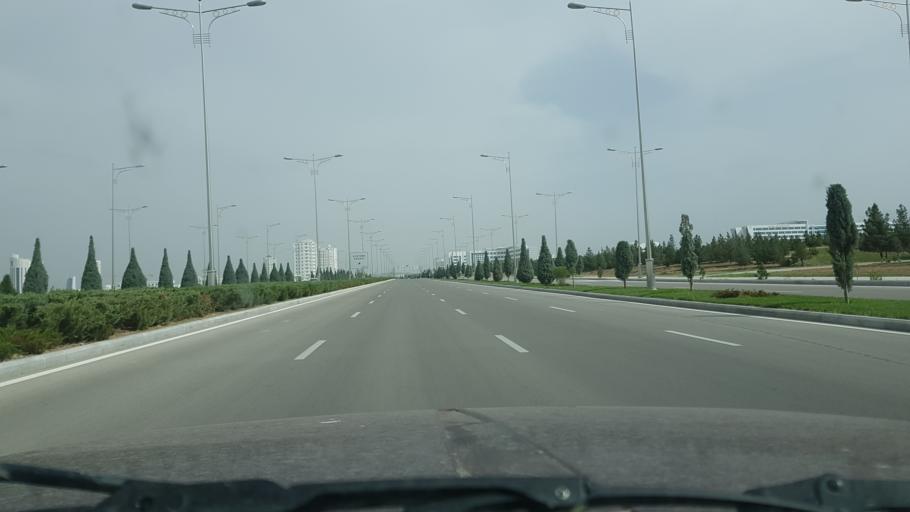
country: TM
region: Ahal
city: Ashgabat
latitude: 37.8825
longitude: 58.3474
